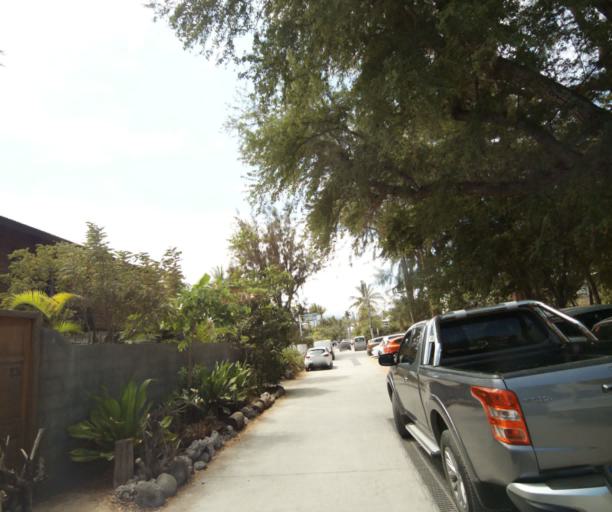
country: RE
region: Reunion
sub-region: Reunion
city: Trois-Bassins
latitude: -21.0935
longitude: 55.2351
